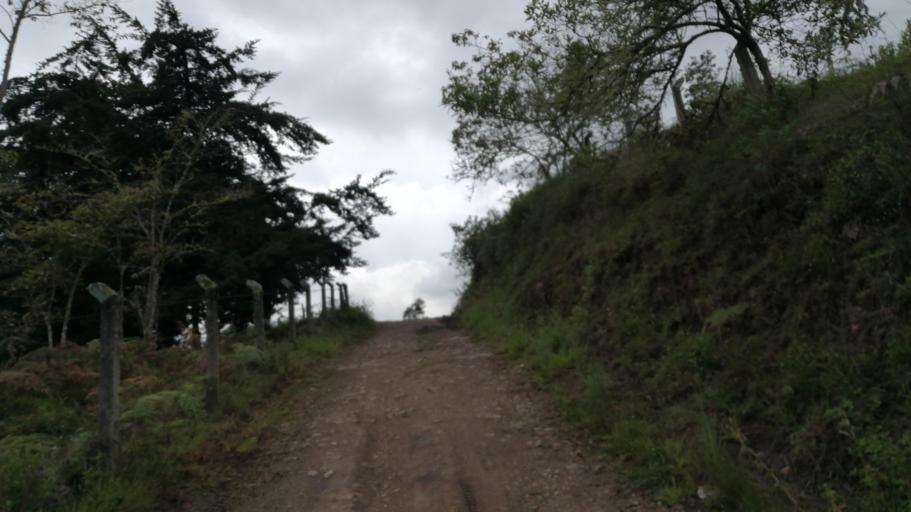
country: CO
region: Boyaca
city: Chinavita
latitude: 5.1350
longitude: -73.3868
